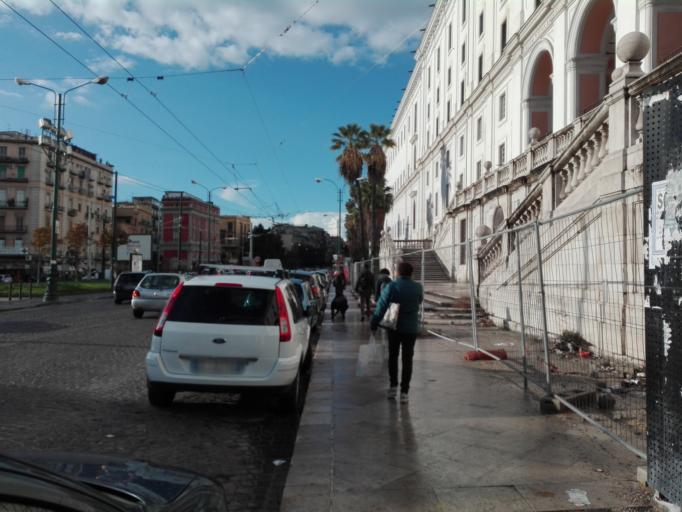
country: IT
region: Campania
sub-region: Provincia di Napoli
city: Napoli
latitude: 40.8633
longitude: 14.2664
